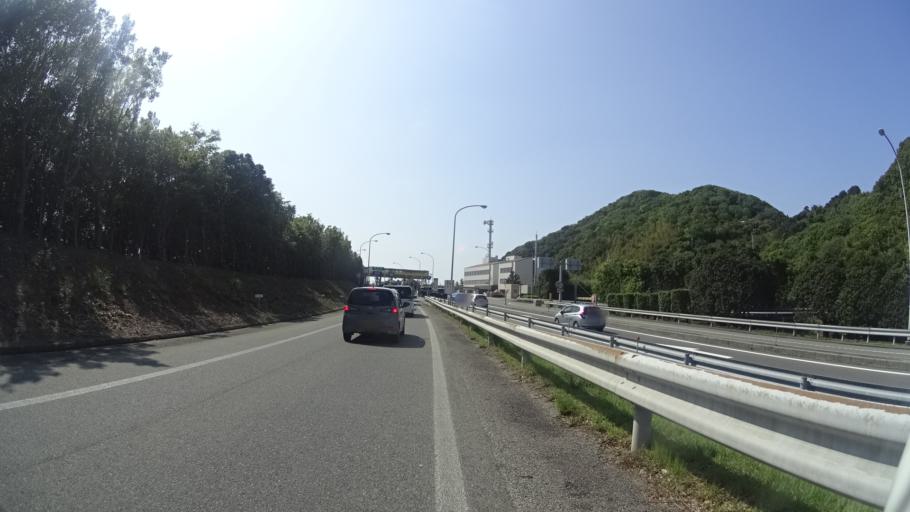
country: JP
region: Tokushima
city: Narutocho-mitsuishi
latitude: 34.2199
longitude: 134.6273
